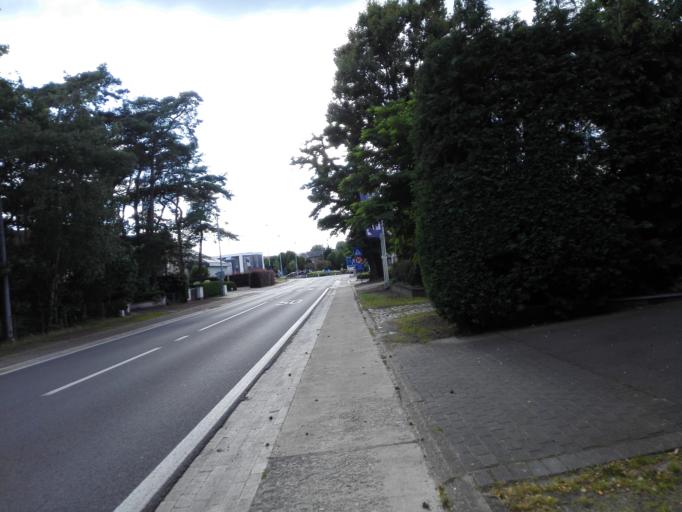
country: BE
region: Flanders
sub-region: Provincie Vlaams-Brabant
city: Keerbergen
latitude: 51.0030
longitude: 4.6372
